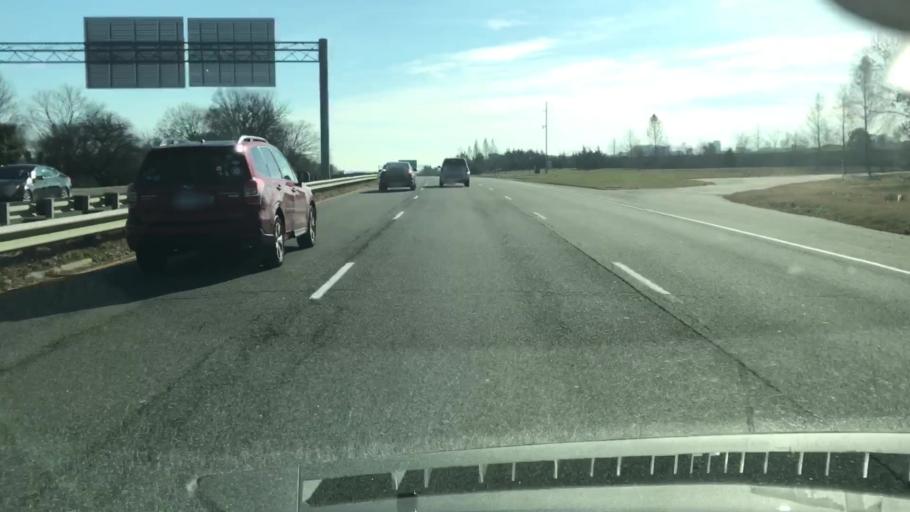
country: US
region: Washington, D.C.
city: Washington, D.C.
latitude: 38.8817
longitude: -77.0619
